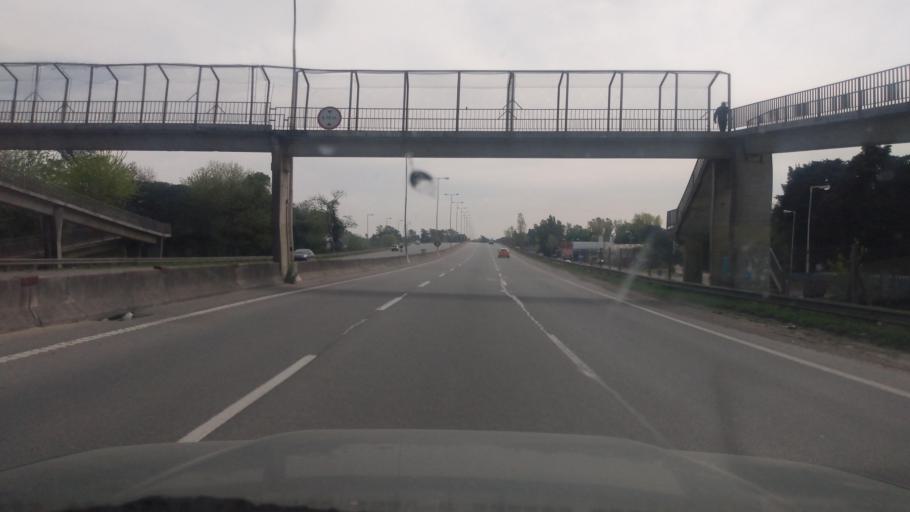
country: AR
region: Buenos Aires
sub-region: Partido de Pilar
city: Pilar
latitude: -34.4343
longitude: -58.9894
